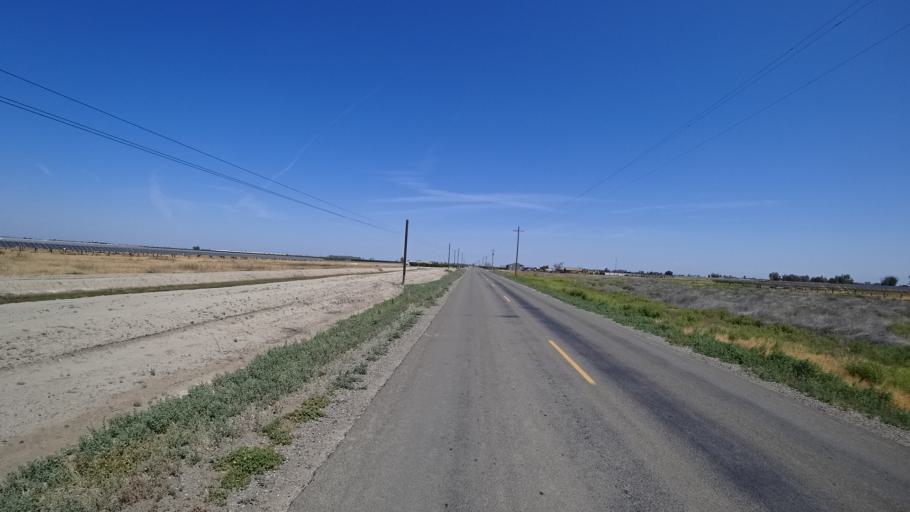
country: US
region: California
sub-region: Kings County
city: Stratford
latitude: 36.2135
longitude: -119.7982
